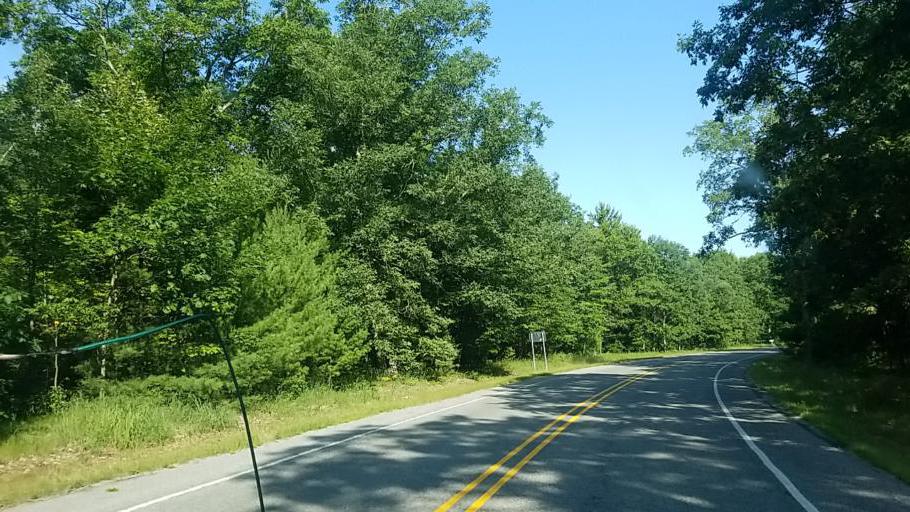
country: US
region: Michigan
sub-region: Muskegon County
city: Lakewood Club
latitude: 43.4653
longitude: -86.2361
